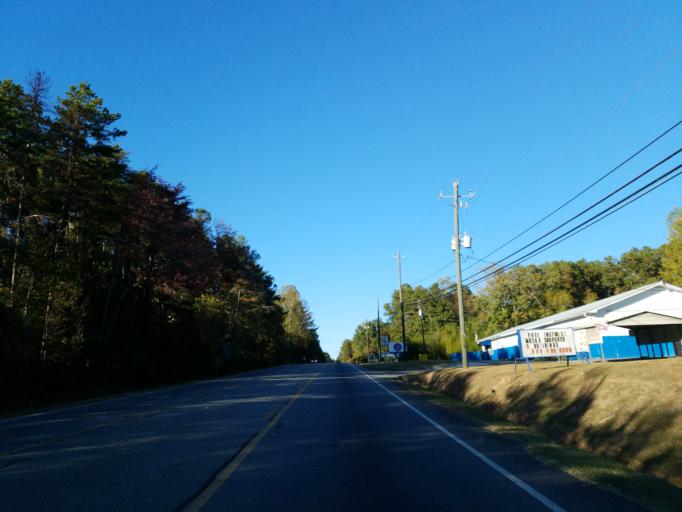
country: US
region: Georgia
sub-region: Cherokee County
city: Ball Ground
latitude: 34.3490
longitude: -84.3797
